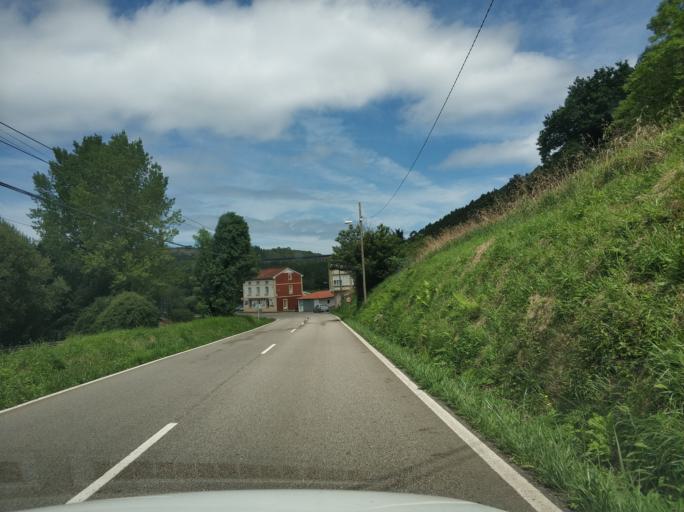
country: ES
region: Asturias
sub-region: Province of Asturias
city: Cudillero
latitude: 43.5572
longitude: -6.2283
